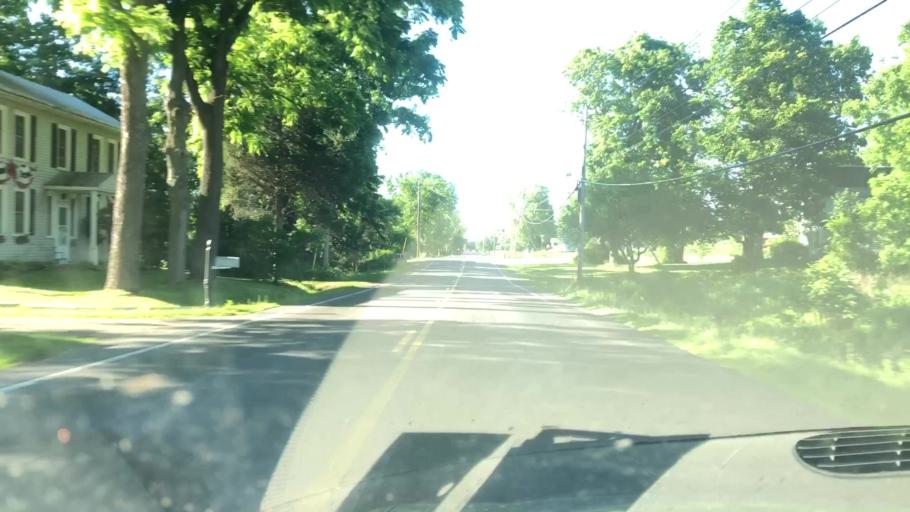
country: US
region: New York
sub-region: Wayne County
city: Macedon
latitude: 43.1154
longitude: -77.3209
